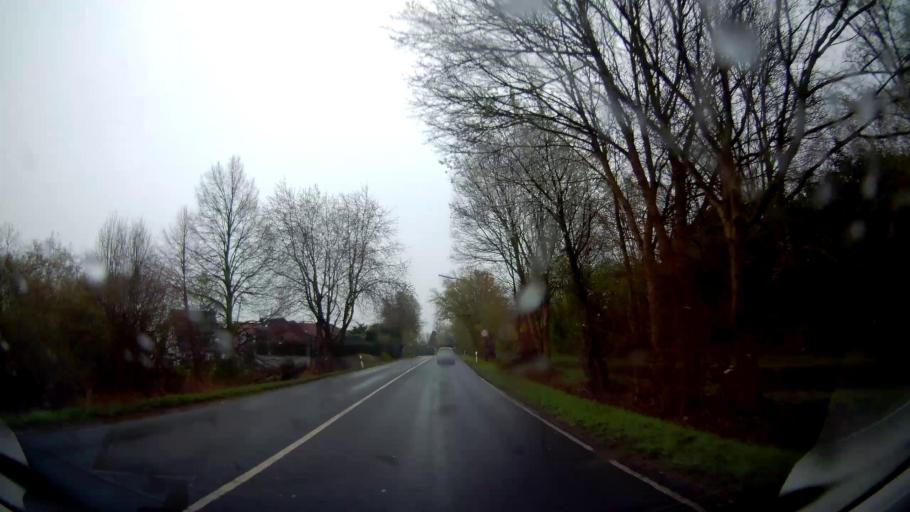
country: DE
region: North Rhine-Westphalia
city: Castrop-Rauxel
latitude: 51.5335
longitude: 7.3441
